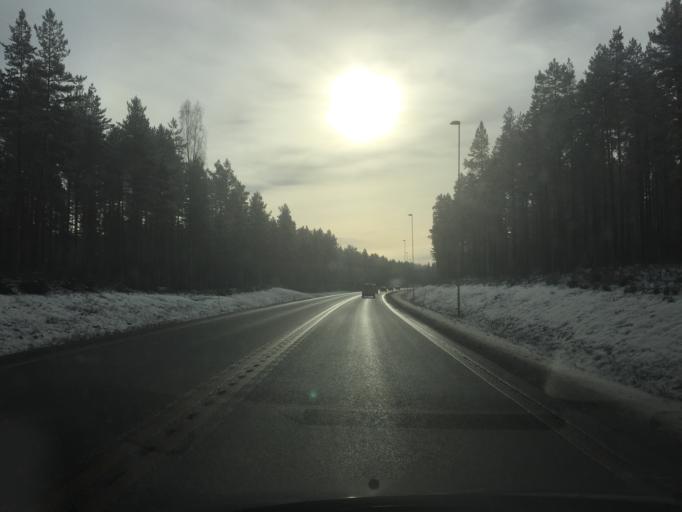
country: NO
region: Hedmark
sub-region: Loten
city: Loten
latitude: 60.7681
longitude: 11.3102
